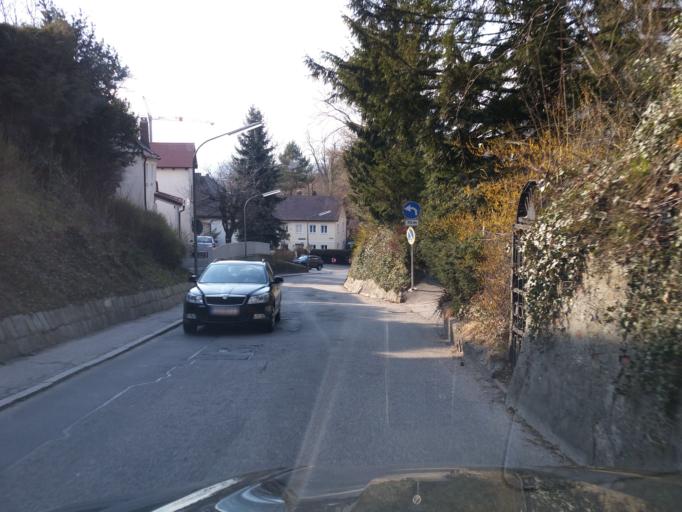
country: DE
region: Bavaria
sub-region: Lower Bavaria
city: Landshut
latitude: 48.5298
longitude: 12.1526
